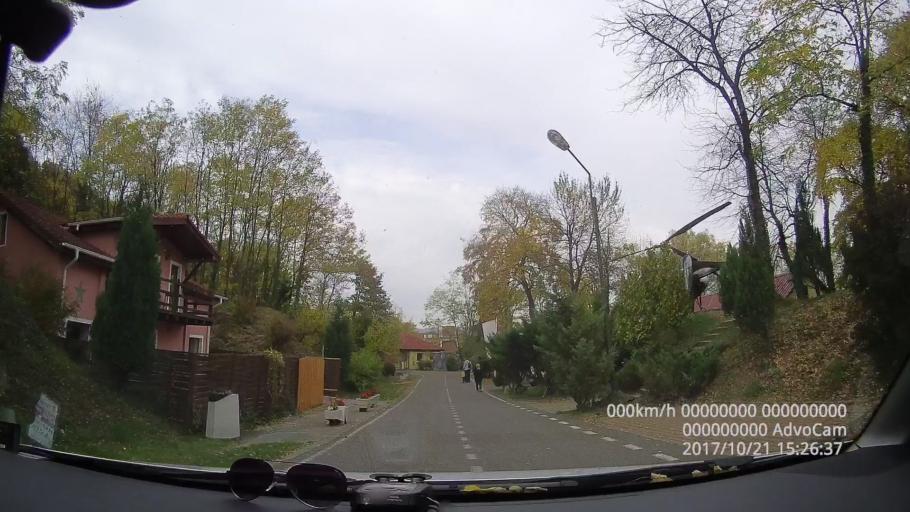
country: RO
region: Hunedoara
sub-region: Municipiul Deva
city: Deva
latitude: 45.8703
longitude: 22.9201
